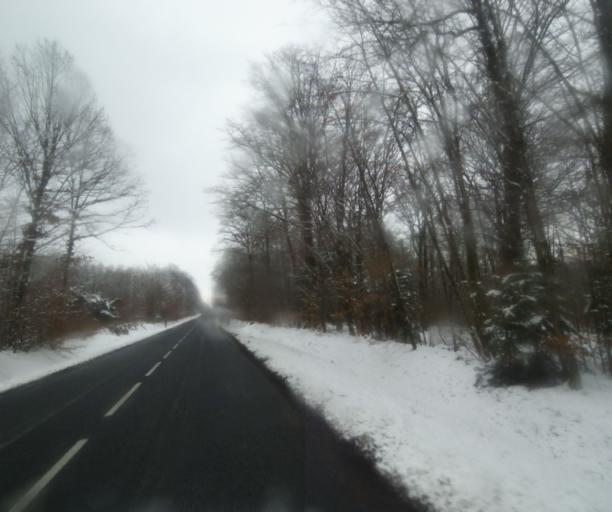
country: FR
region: Champagne-Ardenne
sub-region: Departement de la Haute-Marne
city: Laneuville-a-Remy
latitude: 48.4596
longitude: 4.8918
